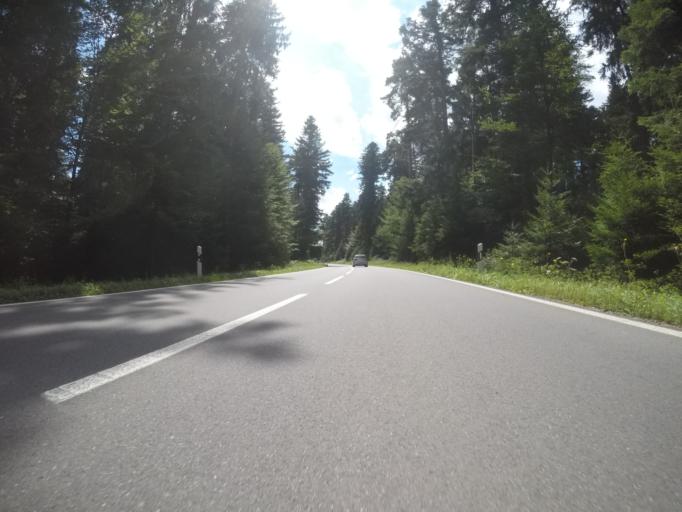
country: DE
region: Baden-Wuerttemberg
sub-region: Karlsruhe Region
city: Neubulach
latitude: 48.6411
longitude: 8.6665
